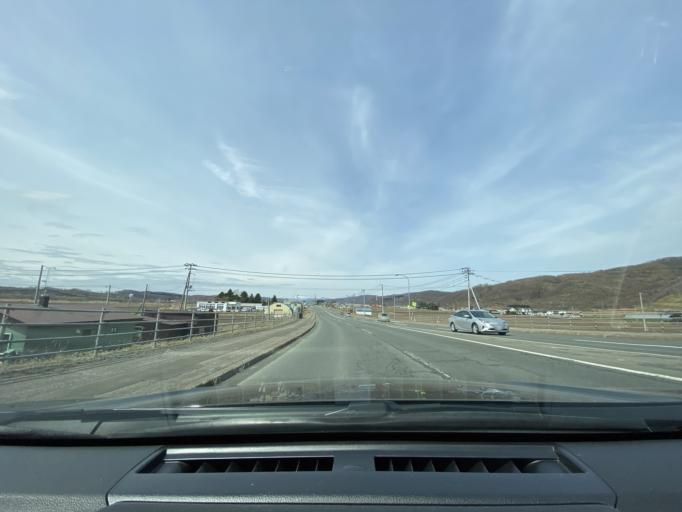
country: JP
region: Hokkaido
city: Kitami
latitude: 43.8012
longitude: 143.7809
